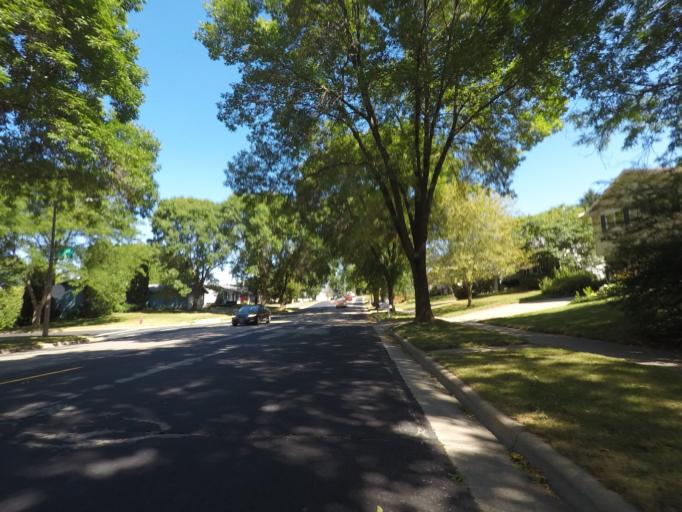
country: US
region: Wisconsin
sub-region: Dane County
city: Verona
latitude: 43.0219
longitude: -89.4987
